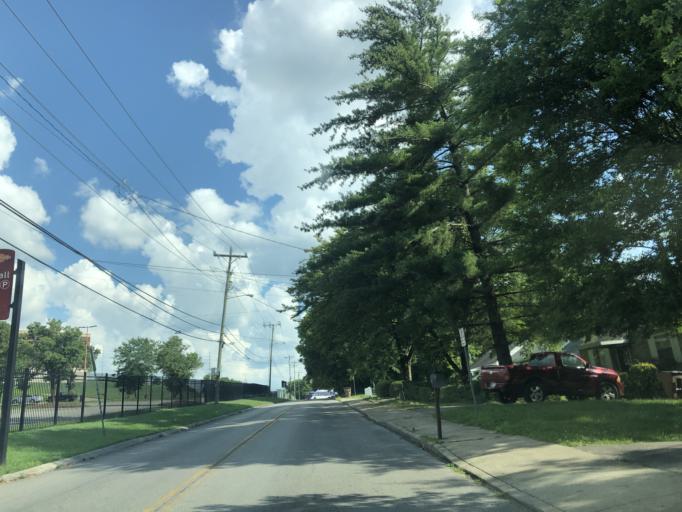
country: US
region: Tennessee
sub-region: Davidson County
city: Nashville
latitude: 36.1655
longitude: -86.8342
